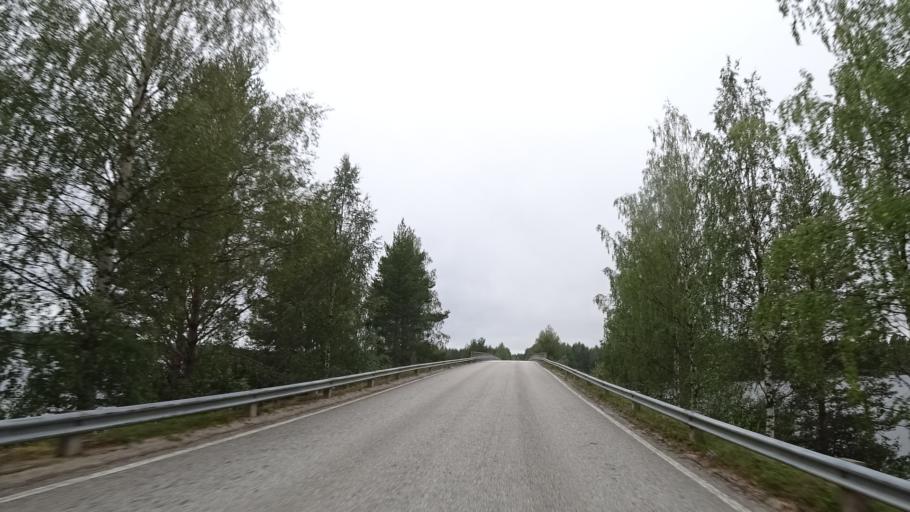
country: FI
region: North Karelia
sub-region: Pielisen Karjala
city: Lieksa
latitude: 63.3479
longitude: 30.2653
